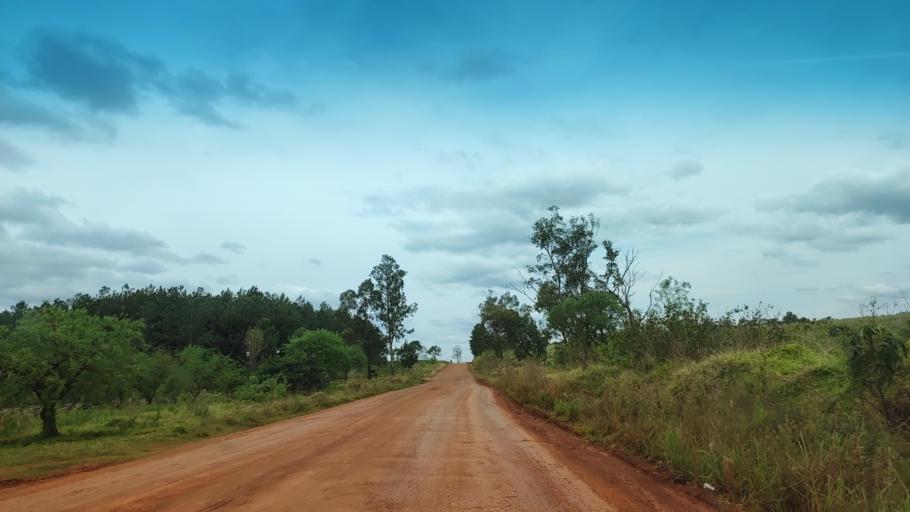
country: AR
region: Misiones
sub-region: Departamento de Capital
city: Posadas
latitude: -27.4804
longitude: -55.9708
